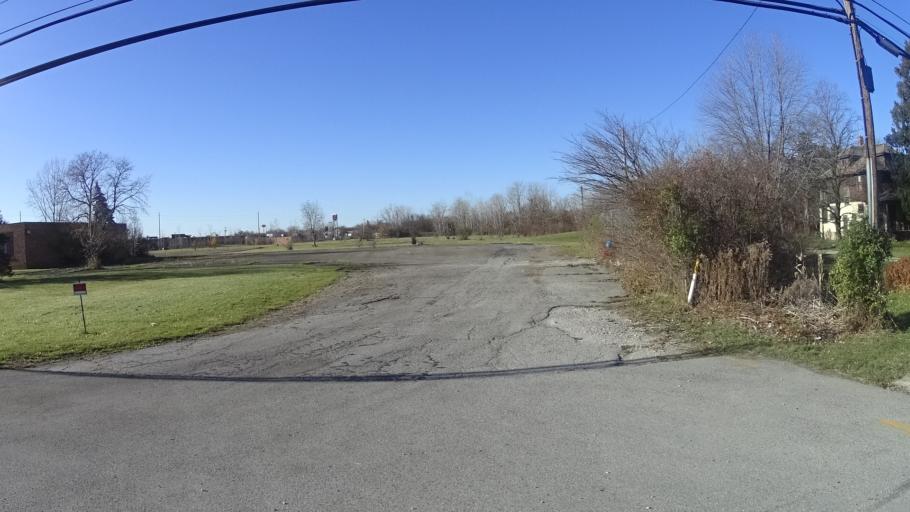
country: US
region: Ohio
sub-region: Lorain County
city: Sheffield
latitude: 41.4031
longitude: -82.1091
